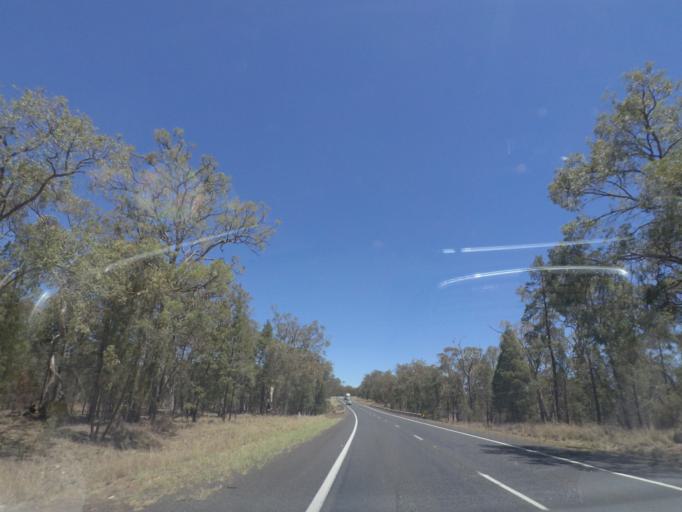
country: AU
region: New South Wales
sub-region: Warrumbungle Shire
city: Coonabarabran
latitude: -31.3453
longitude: 149.2963
